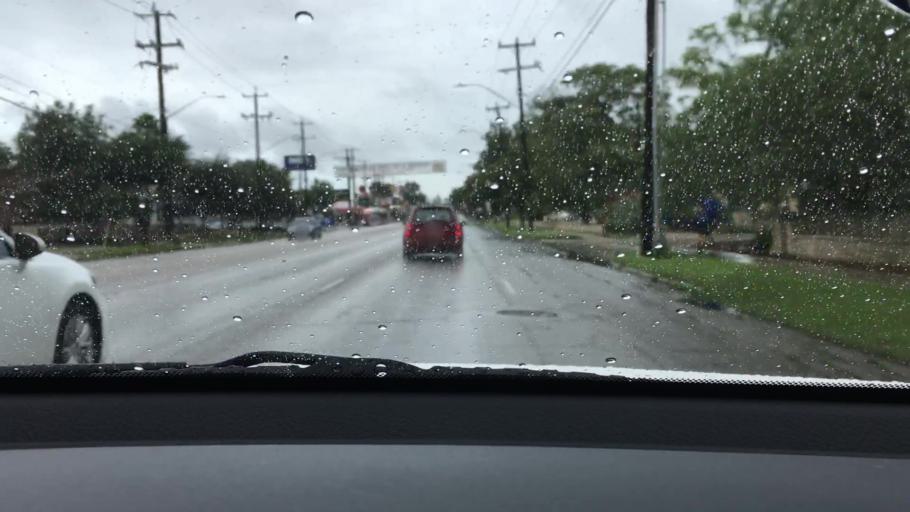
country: US
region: Texas
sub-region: Bexar County
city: Terrell Hills
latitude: 29.4632
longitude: -98.4655
